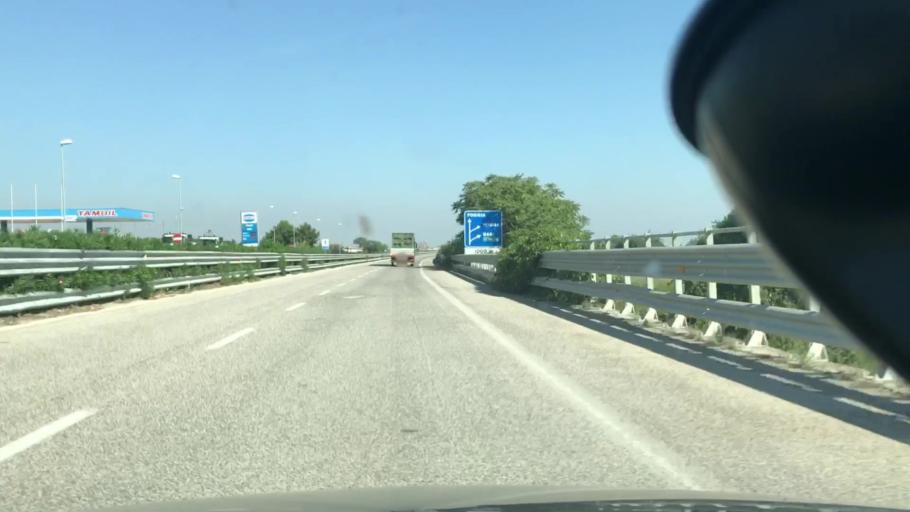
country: IT
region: Apulia
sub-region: Provincia di Foggia
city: Foggia
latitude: 41.4143
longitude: 15.5586
